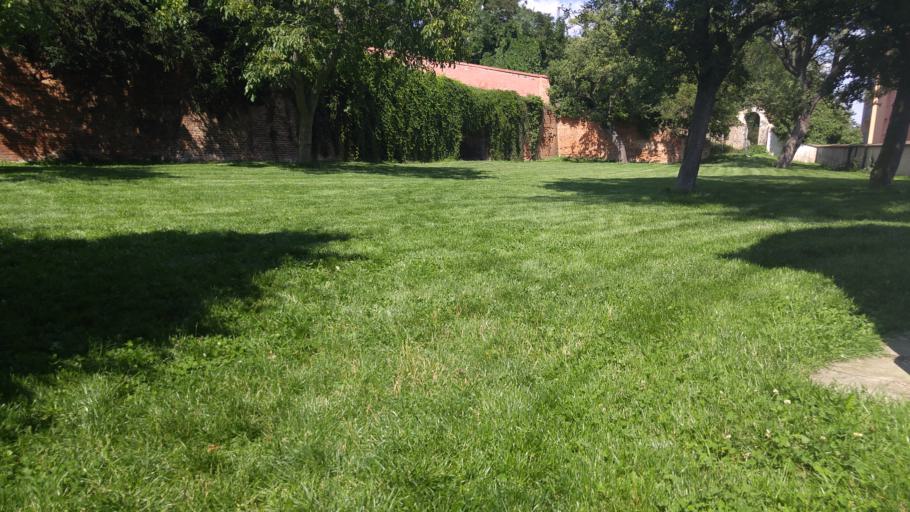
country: CZ
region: Praha
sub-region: Praha 1
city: Mala Strana
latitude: 50.0860
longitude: 14.3598
